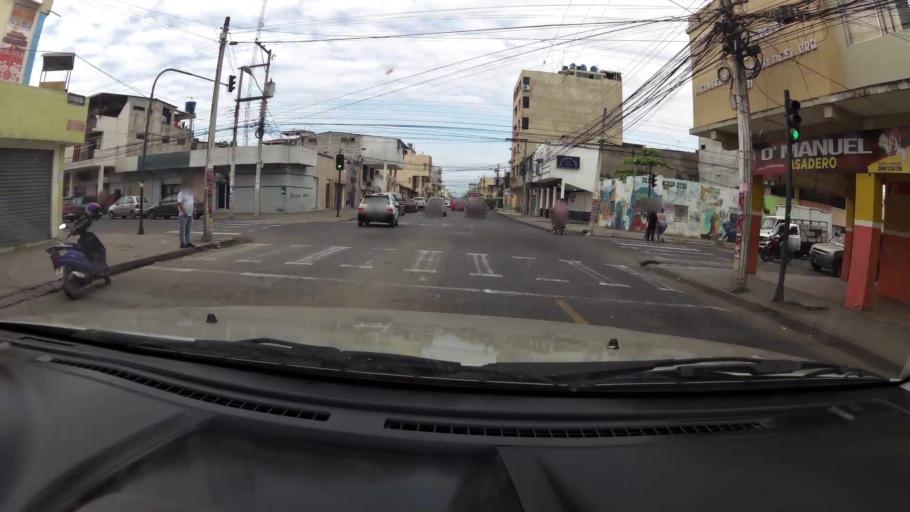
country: EC
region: El Oro
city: Machala
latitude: -3.2546
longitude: -79.9590
